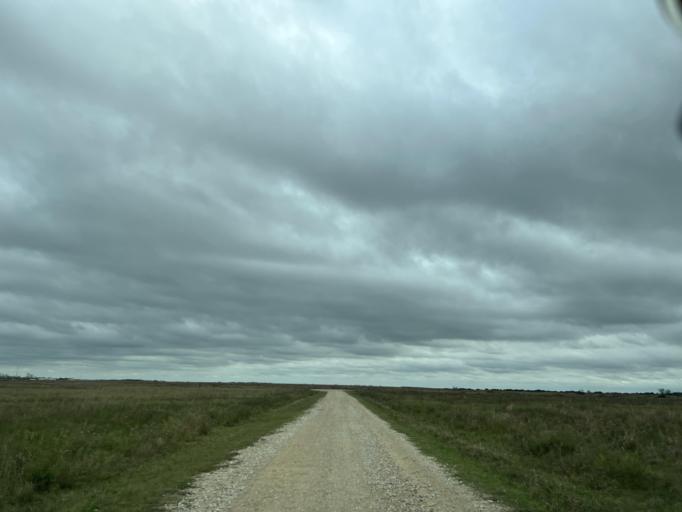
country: US
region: Texas
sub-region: Colorado County
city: Eagle Lake
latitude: 29.6667
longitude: -96.2810
